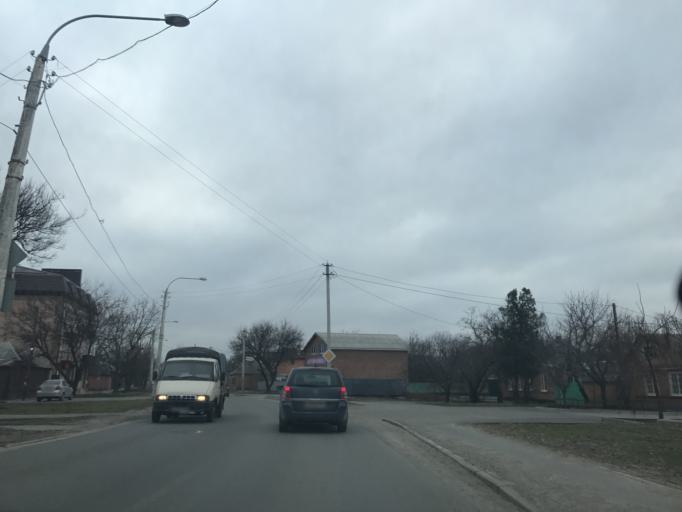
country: RU
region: Rostov
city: Rostov-na-Donu
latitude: 47.2099
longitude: 39.6627
